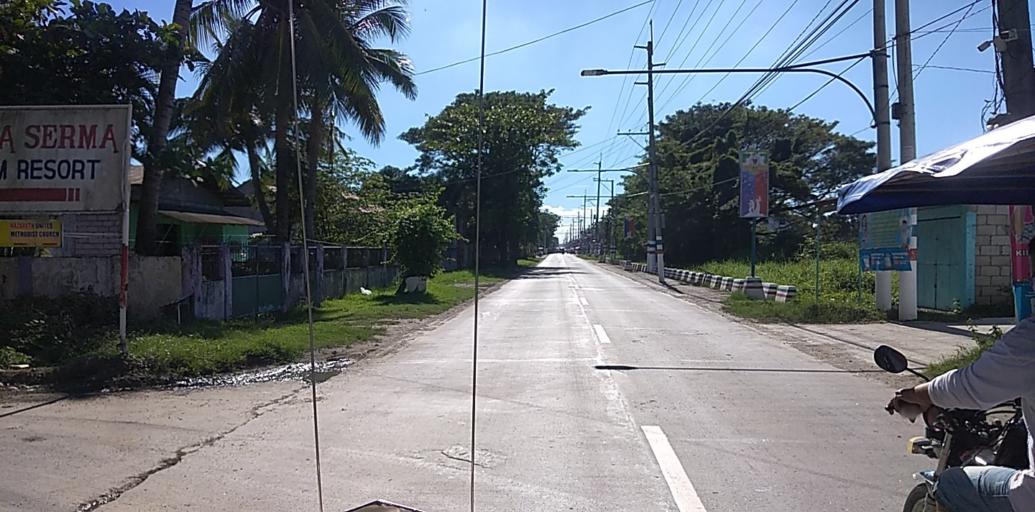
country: PH
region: Central Luzon
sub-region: Province of Pampanga
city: San Luis
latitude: 15.0536
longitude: 120.7794
